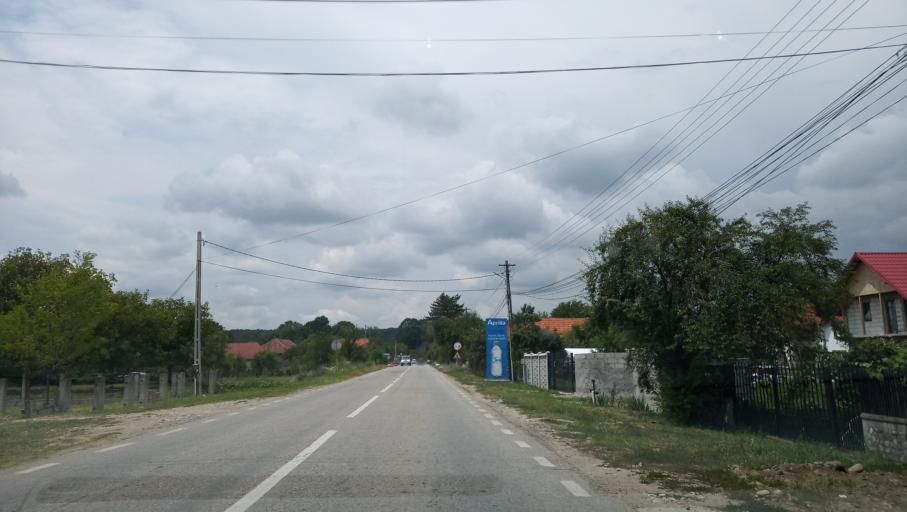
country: RO
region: Gorj
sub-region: Comuna Arcani
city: Arcani
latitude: 45.0886
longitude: 23.1390
